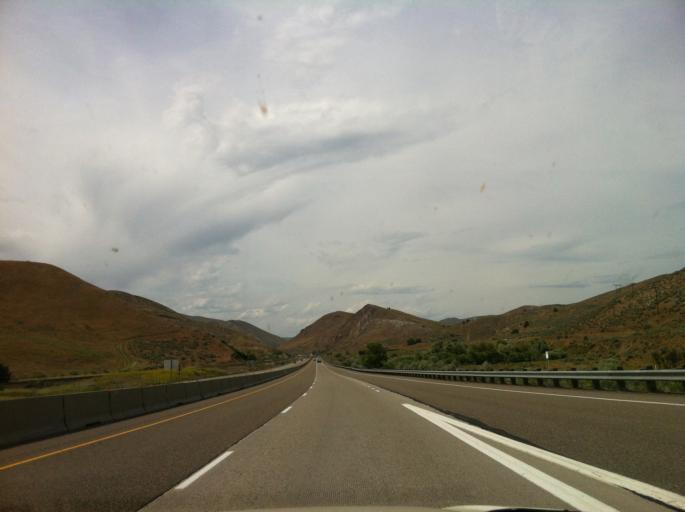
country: US
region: Idaho
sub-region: Washington County
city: Weiser
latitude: 44.3800
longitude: -117.3020
